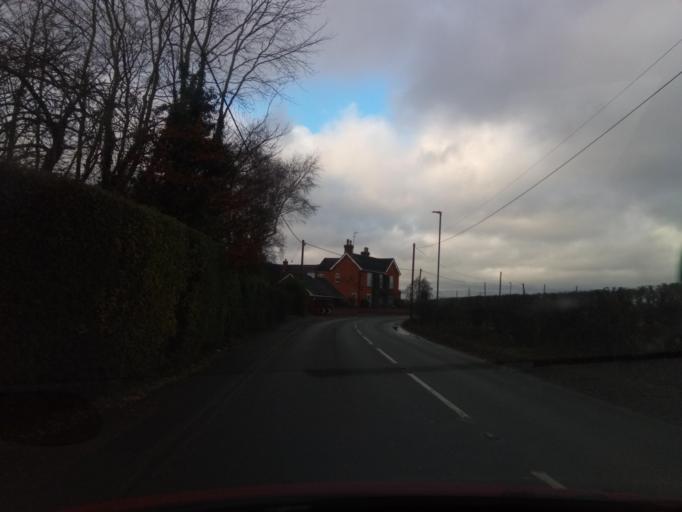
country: GB
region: England
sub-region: Derbyshire
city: Melbourne
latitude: 52.8306
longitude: -1.4367
